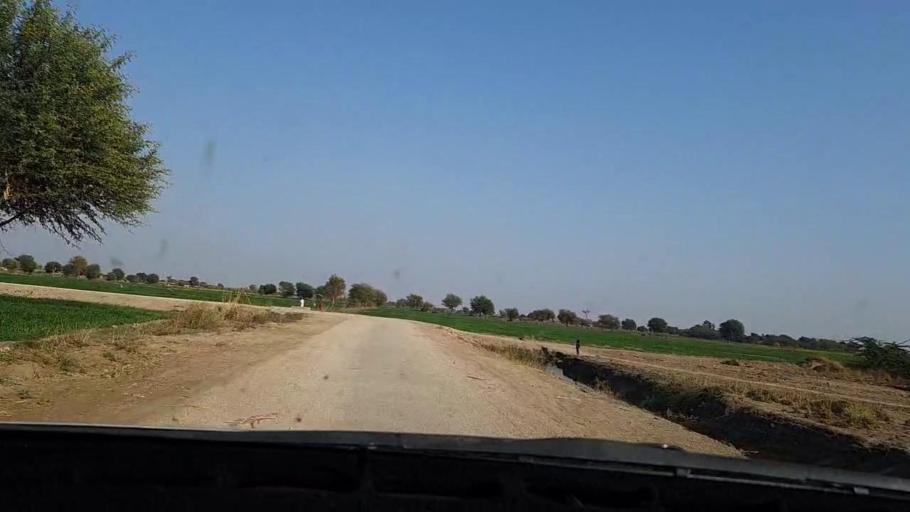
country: PK
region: Sindh
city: Tando Mittha Khan
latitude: 25.8283
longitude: 69.3119
